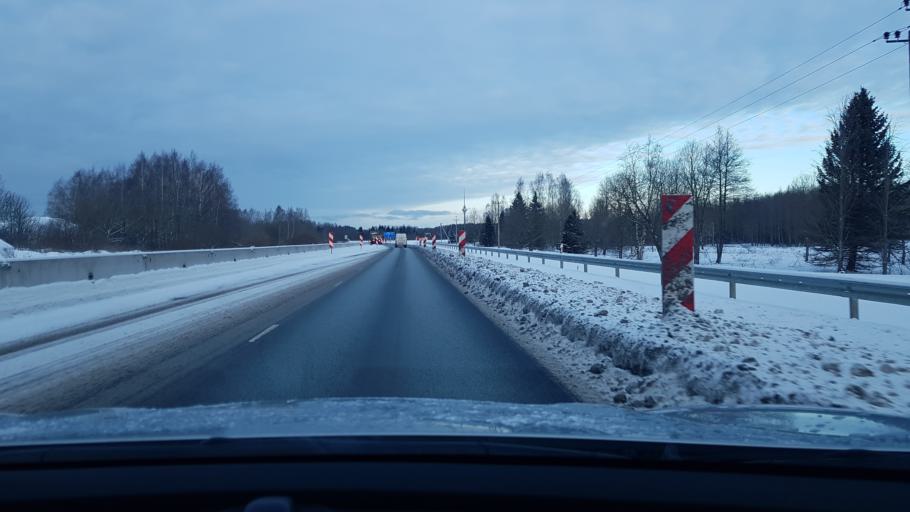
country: EE
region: Harju
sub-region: Joelaehtme vald
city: Loo
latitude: 59.4375
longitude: 24.9138
